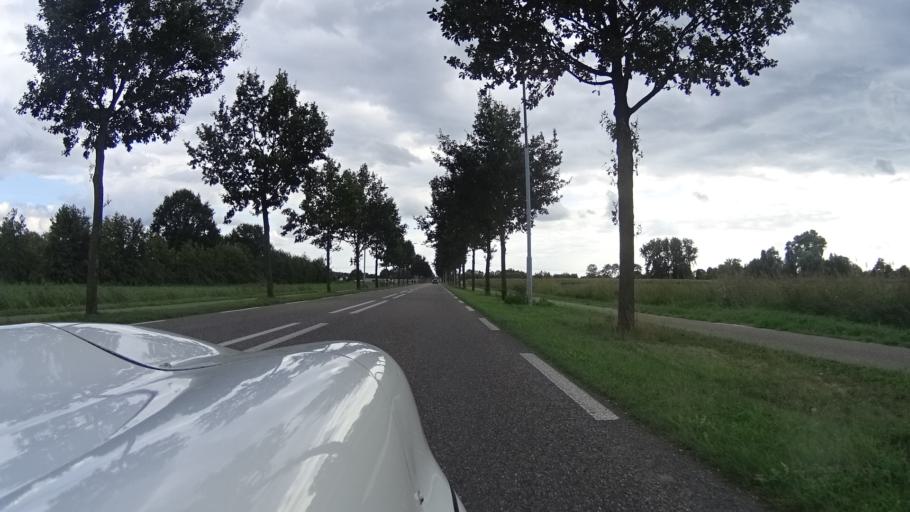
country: NL
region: North Brabant
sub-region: Gemeente Heusden
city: Heusden
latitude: 51.7160
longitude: 5.1817
